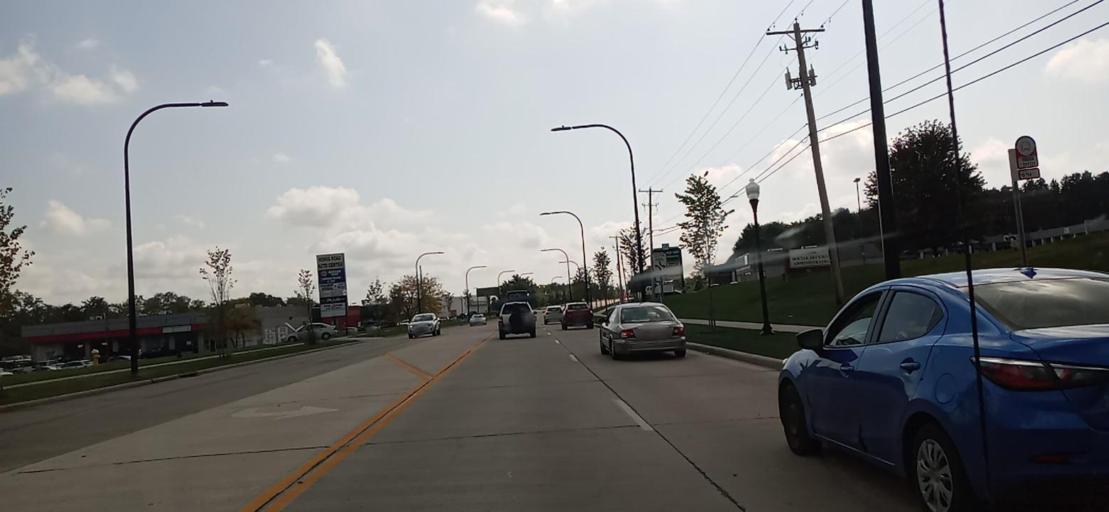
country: US
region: Ohio
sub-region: Summit County
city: Barberton
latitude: 41.0567
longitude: -81.5811
